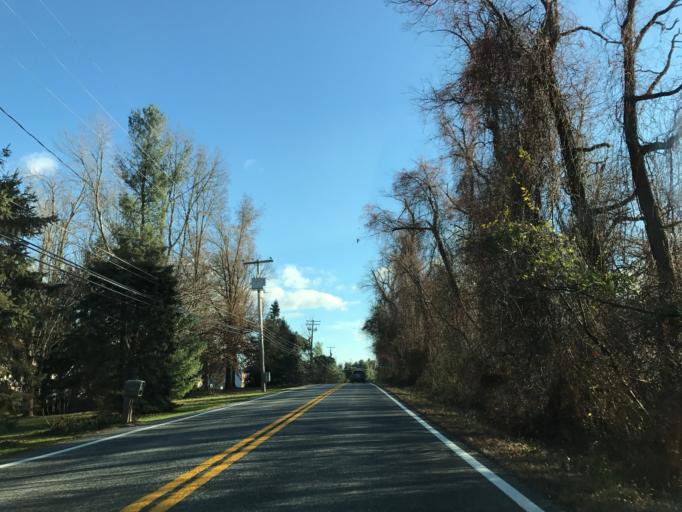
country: US
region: Maryland
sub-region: Harford County
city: Jarrettsville
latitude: 39.5820
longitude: -76.5020
